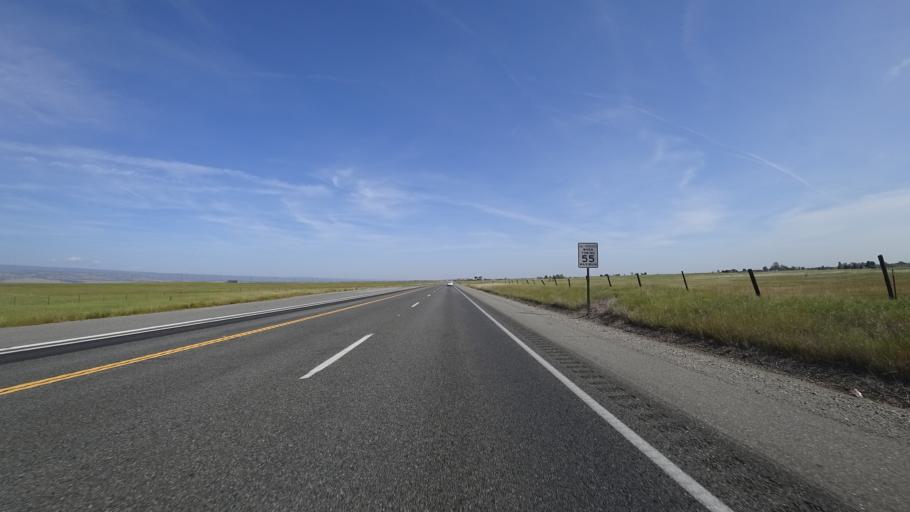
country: US
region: California
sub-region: Tehama County
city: Los Molinos
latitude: 39.9256
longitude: -122.0259
